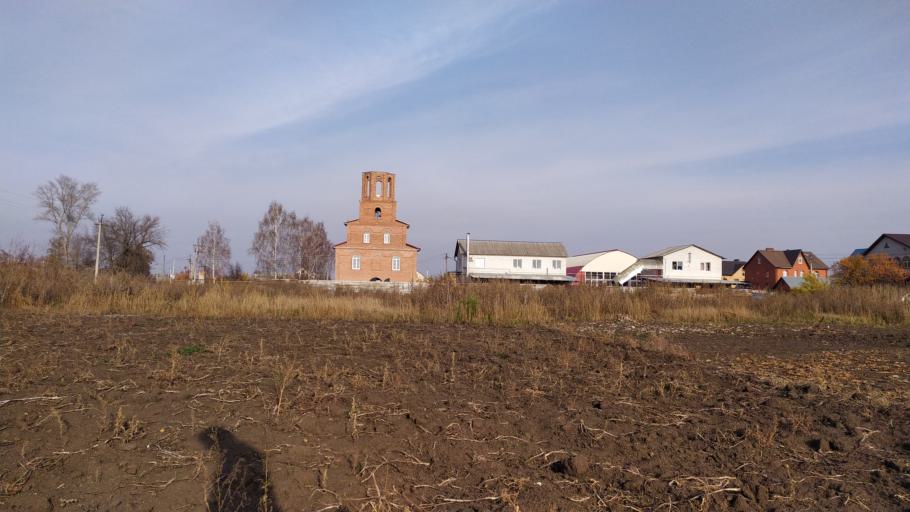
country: RU
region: Kursk
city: Kursk
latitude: 51.6410
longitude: 36.1492
